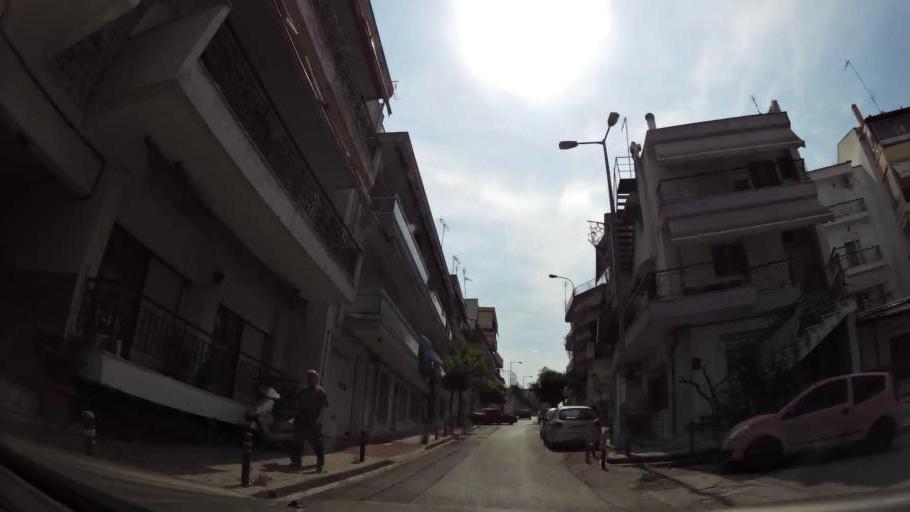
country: GR
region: Central Macedonia
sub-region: Nomos Thessalonikis
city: Sykies
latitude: 40.6490
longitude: 22.9568
